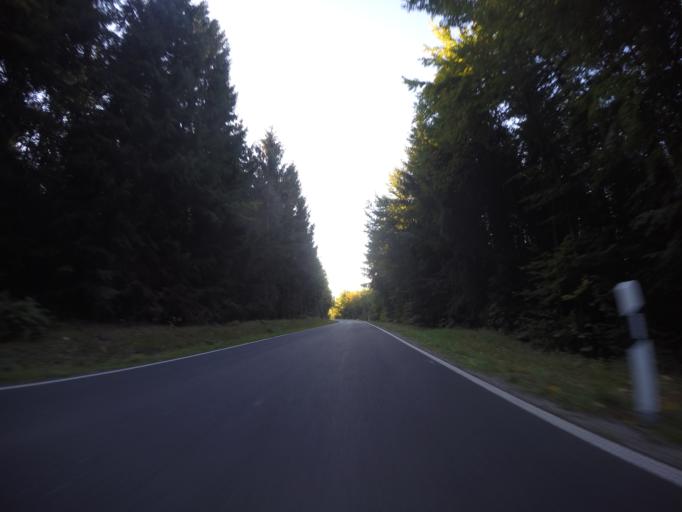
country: DE
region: Bavaria
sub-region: Regierungsbezirk Unterfranken
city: Altenbuch
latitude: 49.8646
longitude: 9.4159
